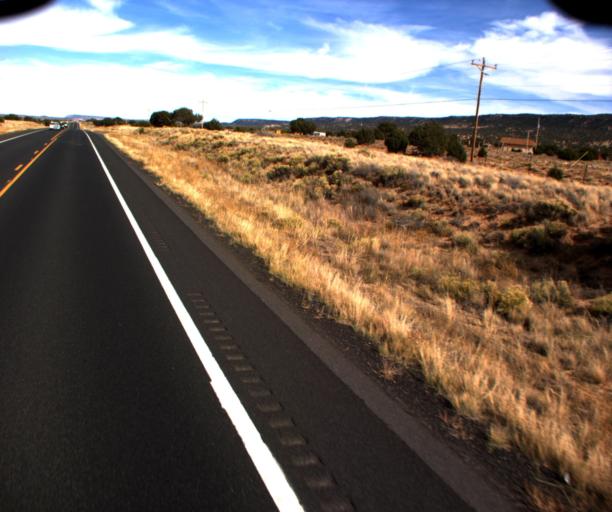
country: US
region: Arizona
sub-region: Navajo County
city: Kayenta
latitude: 36.4967
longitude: -110.6234
